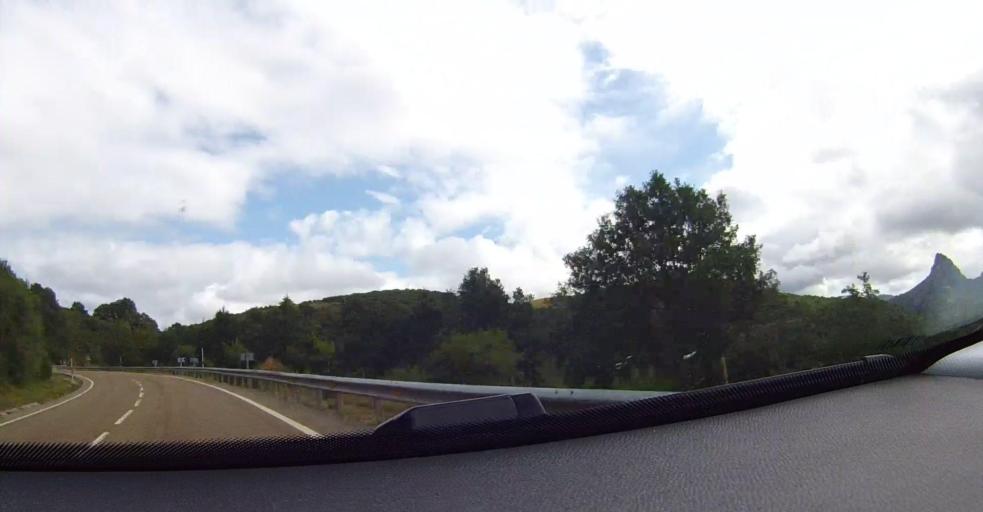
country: ES
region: Castille and Leon
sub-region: Provincia de Leon
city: Riano
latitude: 42.9817
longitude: -4.9943
